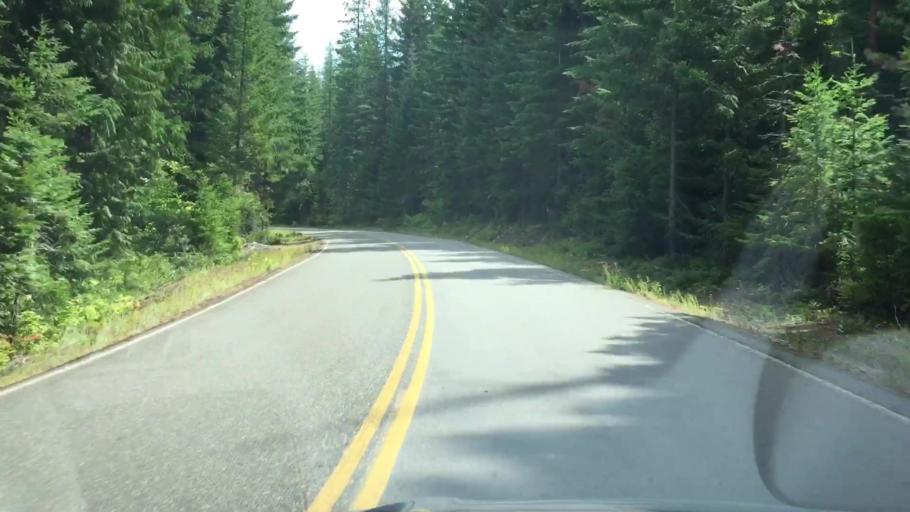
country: US
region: Washington
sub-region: Klickitat County
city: White Salmon
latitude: 46.1071
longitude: -121.6142
